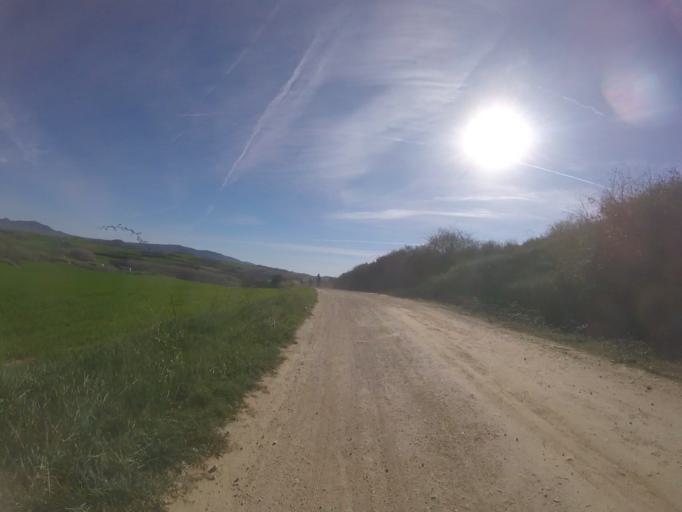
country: ES
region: Navarre
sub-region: Provincia de Navarra
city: Villatuerta
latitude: 42.6928
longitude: -2.0012
